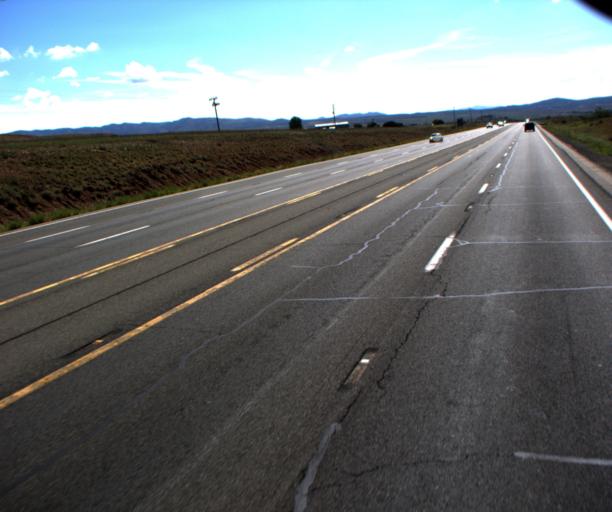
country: US
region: Arizona
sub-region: Yavapai County
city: Prescott Valley
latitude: 34.5778
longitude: -112.2931
